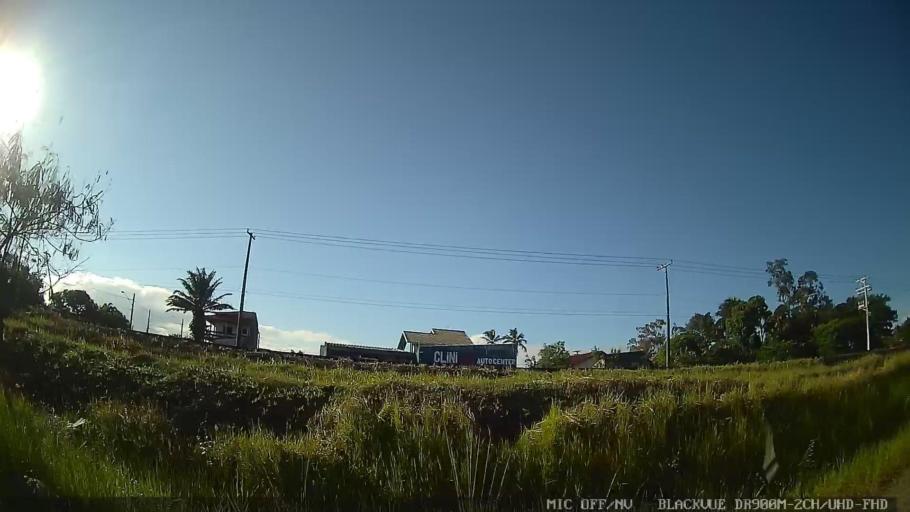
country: BR
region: Sao Paulo
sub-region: Peruibe
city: Peruibe
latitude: -24.2999
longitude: -46.9855
